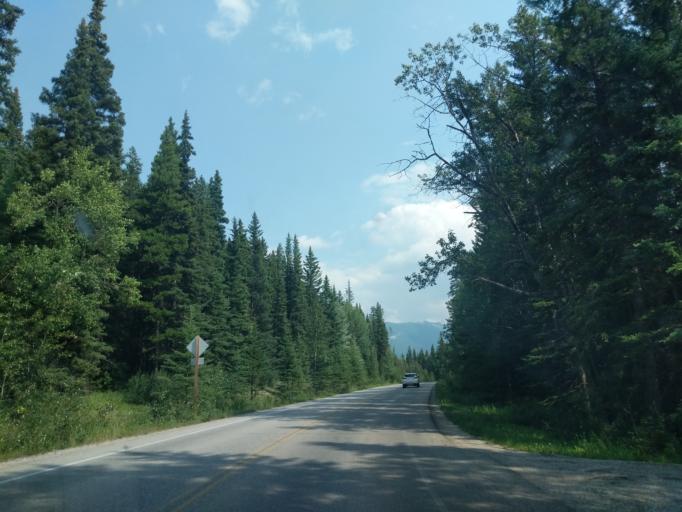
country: CA
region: Alberta
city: Banff
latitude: 51.1689
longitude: -115.6812
